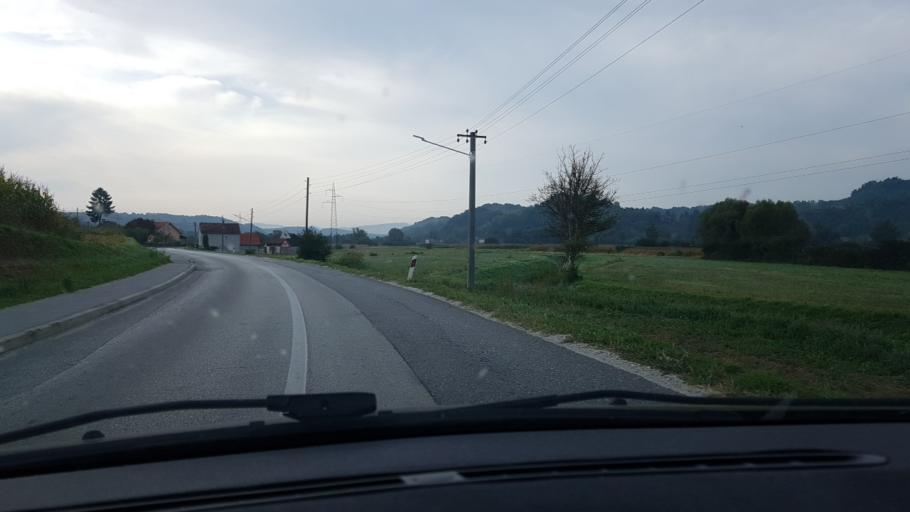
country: HR
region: Krapinsko-Zagorska
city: Zlatar
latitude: 46.0978
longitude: 16.0356
